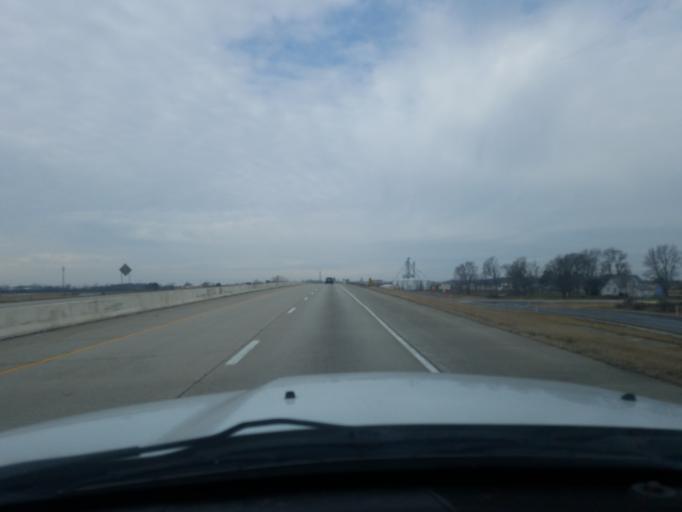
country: US
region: Indiana
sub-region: Huntington County
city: Roanoke
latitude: 40.9585
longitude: -85.2709
